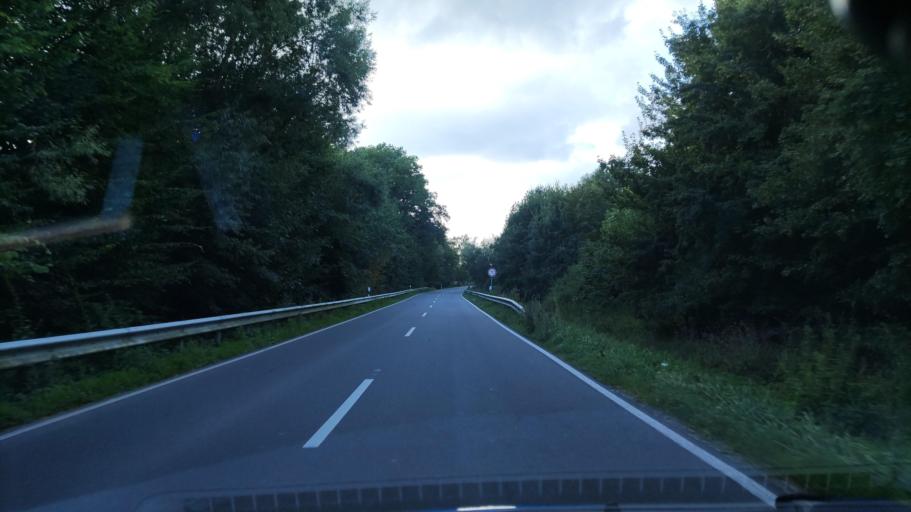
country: DE
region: Schleswig-Holstein
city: Ahrensbok
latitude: 54.0336
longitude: 10.5508
